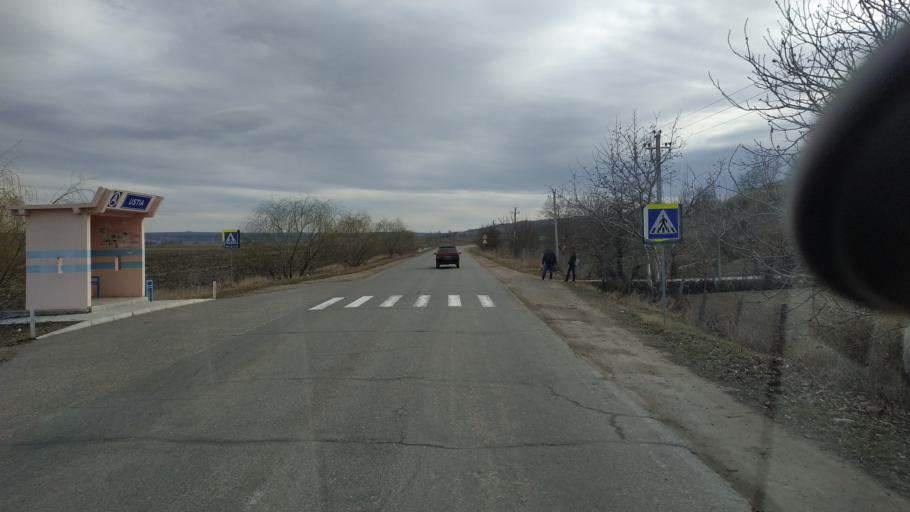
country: MD
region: Telenesti
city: Dubasari
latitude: 47.2563
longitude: 29.1344
